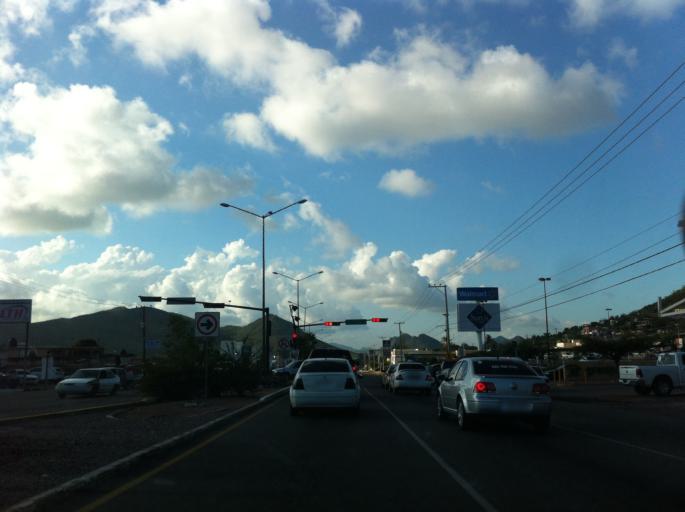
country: MX
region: Sonora
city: Heroica Guaymas
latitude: 27.9345
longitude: -110.9275
